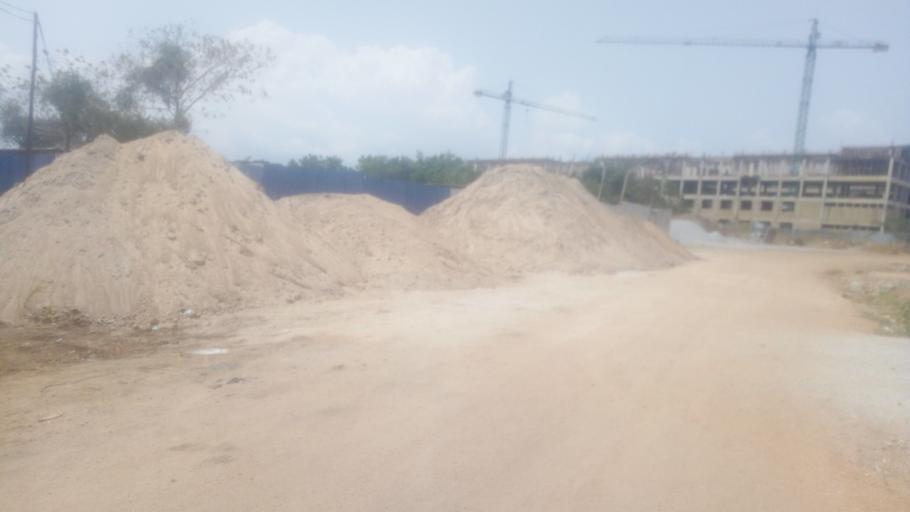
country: GH
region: Central
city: Winneba
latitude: 5.3699
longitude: -0.6329
